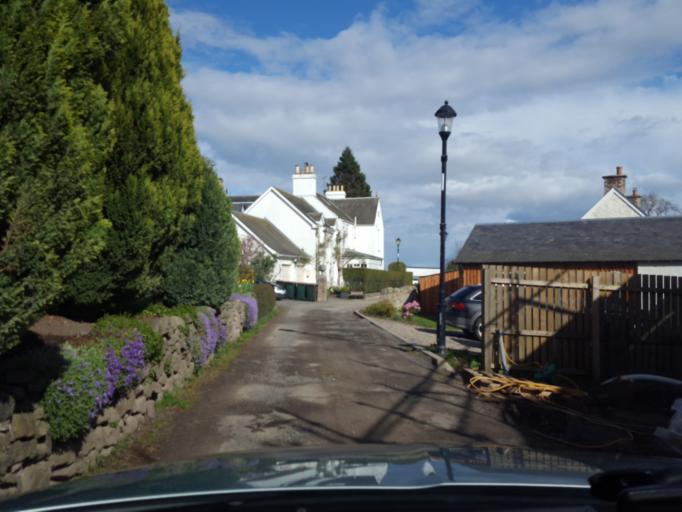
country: GB
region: Scotland
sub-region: Perth and Kinross
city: Errol
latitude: 56.4275
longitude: -3.2566
